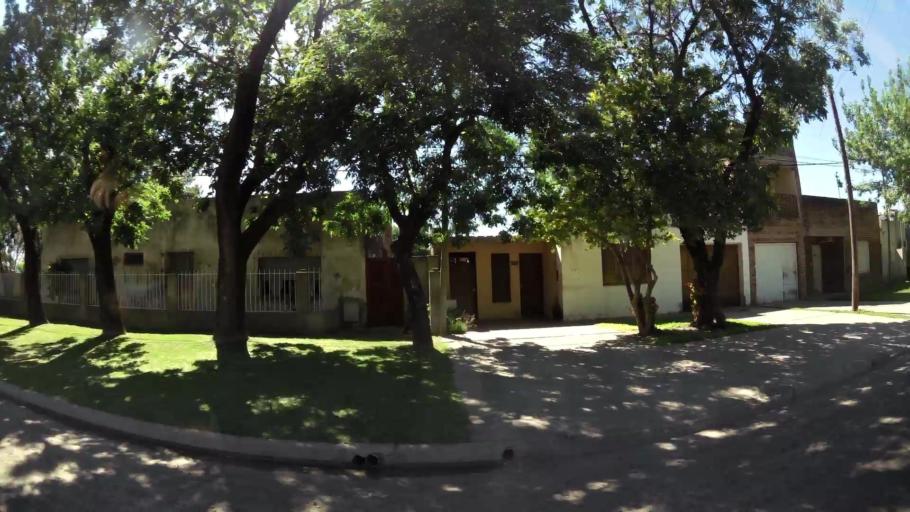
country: AR
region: Santa Fe
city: Esperanza
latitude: -31.4644
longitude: -60.9350
